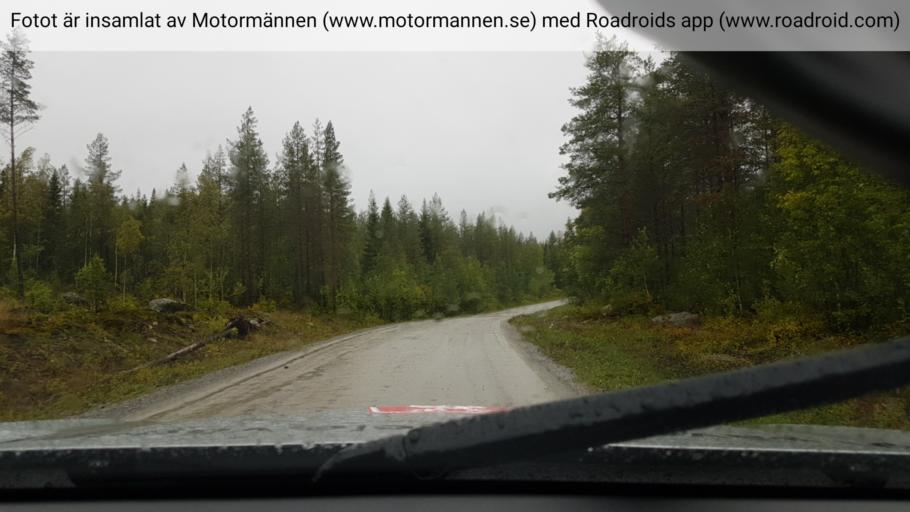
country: SE
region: Vaesternorrland
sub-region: OErnskoeldsviks Kommun
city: Bredbyn
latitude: 64.0625
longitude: 18.0980
